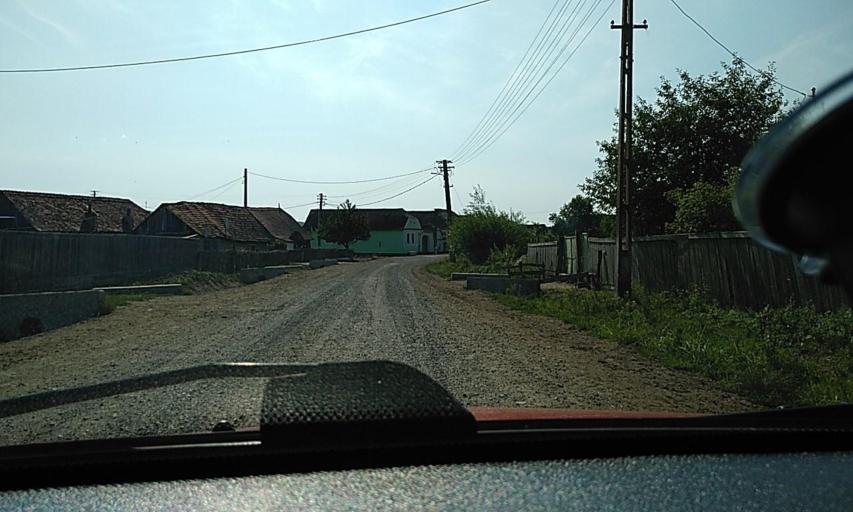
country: RO
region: Brasov
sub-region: Oras Rupea
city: Fiser
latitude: 46.0582
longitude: 25.0955
